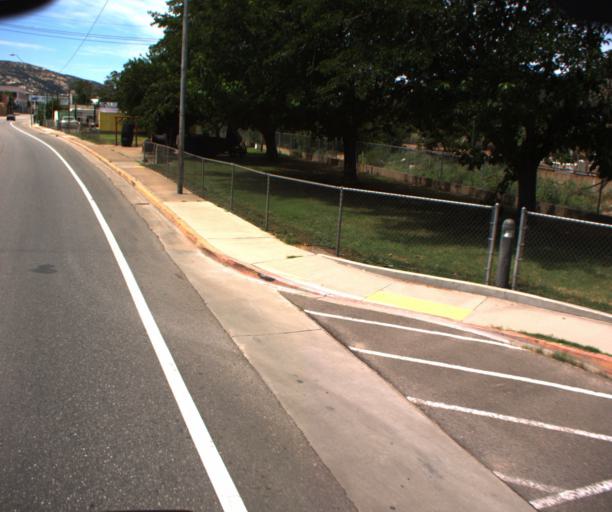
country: US
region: Arizona
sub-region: Gila County
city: Miami
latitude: 33.4008
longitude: -110.8673
